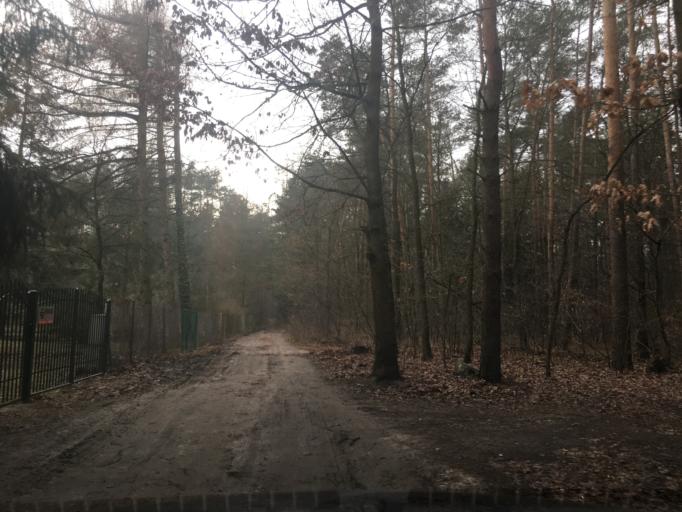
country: PL
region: Masovian Voivodeship
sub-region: Powiat piaseczynski
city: Lesznowola
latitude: 52.0783
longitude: 20.9189
